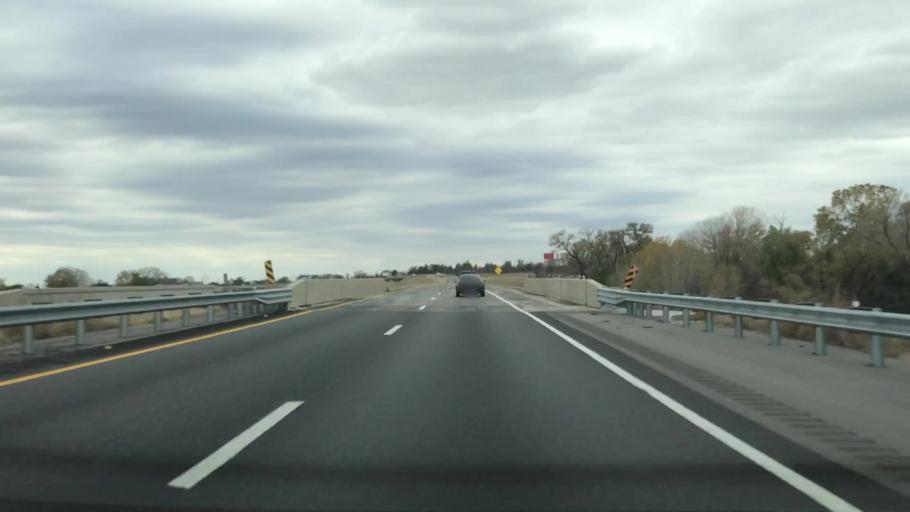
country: US
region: Oklahoma
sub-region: Beckham County
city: Elk City
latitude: 35.3858
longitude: -99.5051
